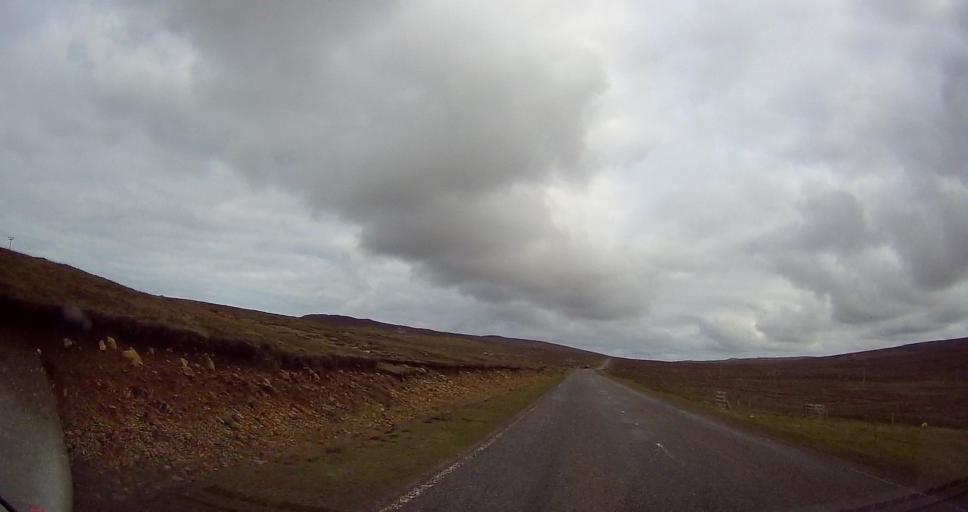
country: GB
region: Scotland
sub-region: Shetland Islands
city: Shetland
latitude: 60.7020
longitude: -0.9203
